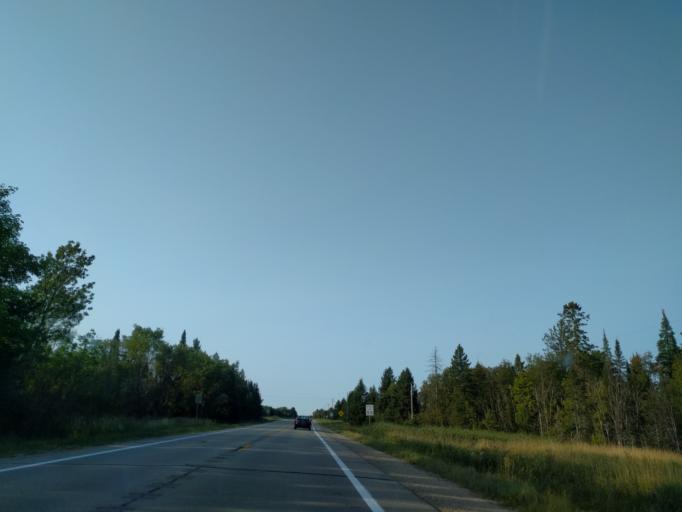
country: US
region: Michigan
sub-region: Delta County
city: Gladstone
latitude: 46.0761
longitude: -86.9809
